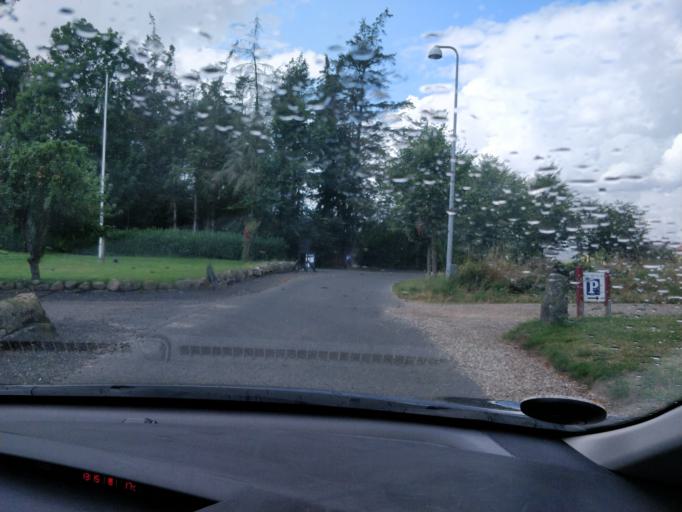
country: DK
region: South Denmark
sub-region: Assens Kommune
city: Assens
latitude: 55.2599
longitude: 9.7374
